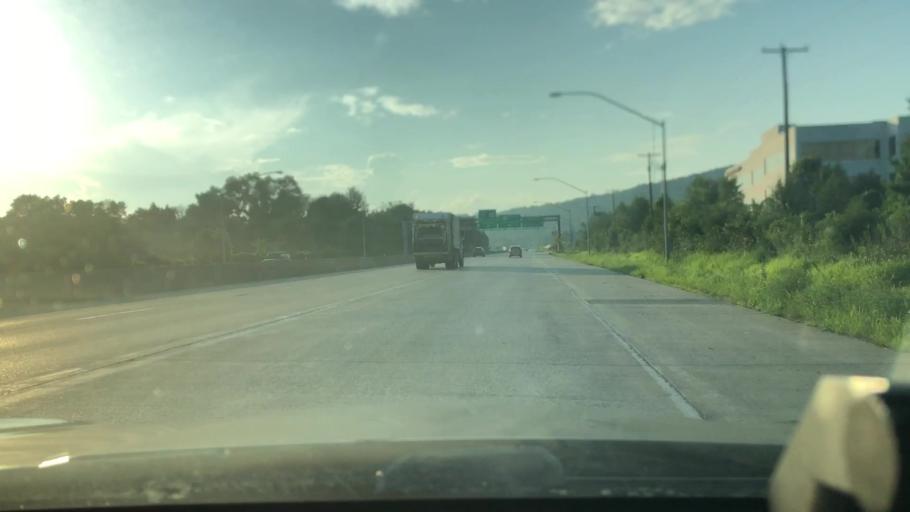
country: US
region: Pennsylvania
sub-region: Lehigh County
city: Coopersburg
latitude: 40.5495
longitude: -75.4255
